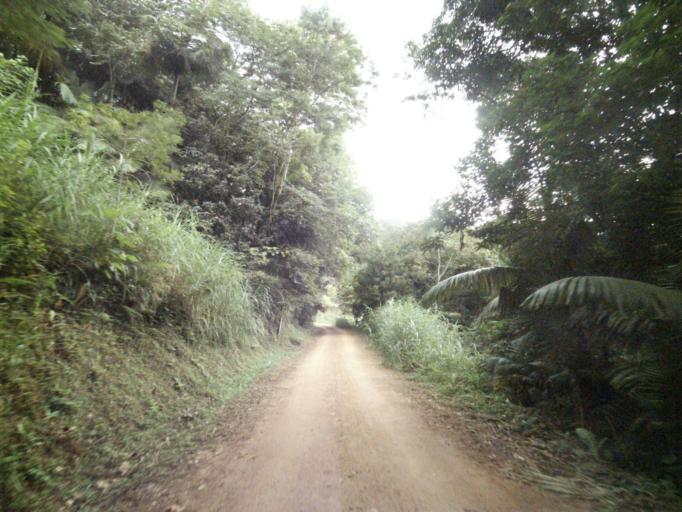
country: BR
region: Santa Catarina
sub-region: Pomerode
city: Pomerode
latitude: -26.7363
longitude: -49.1959
